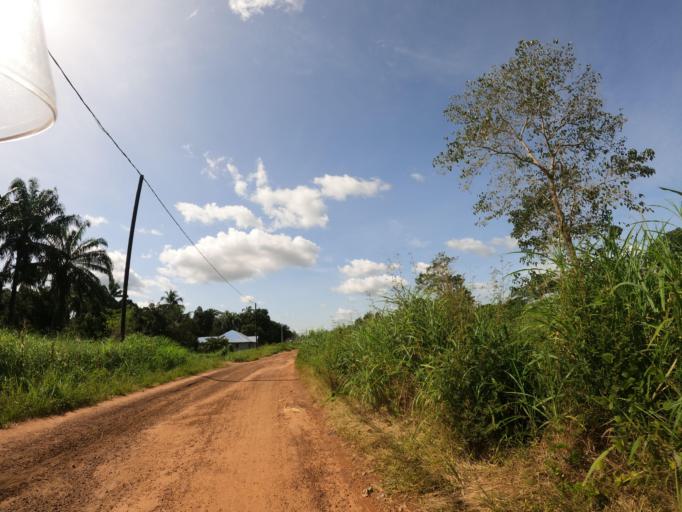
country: SL
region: Northern Province
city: Makeni
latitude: 8.8538
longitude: -12.0245
